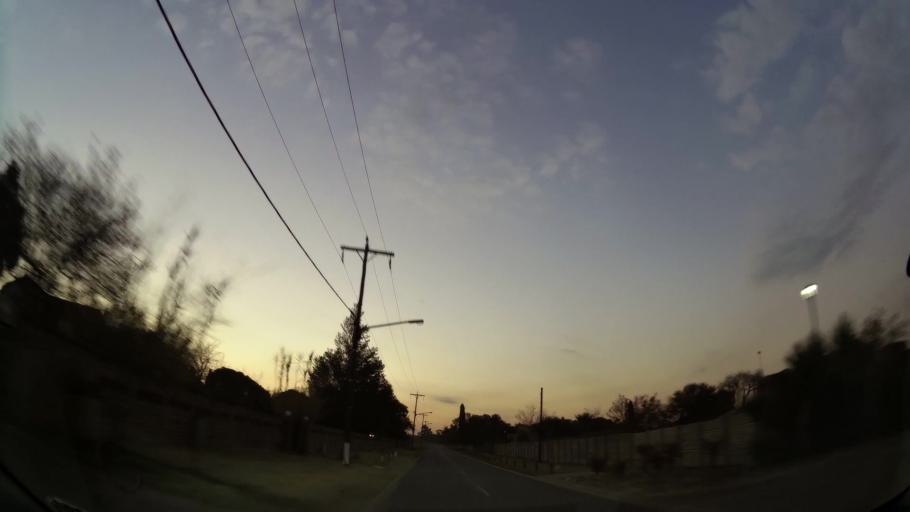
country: ZA
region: Gauteng
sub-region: Ekurhuleni Metropolitan Municipality
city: Benoni
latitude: -26.1264
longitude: 28.3074
